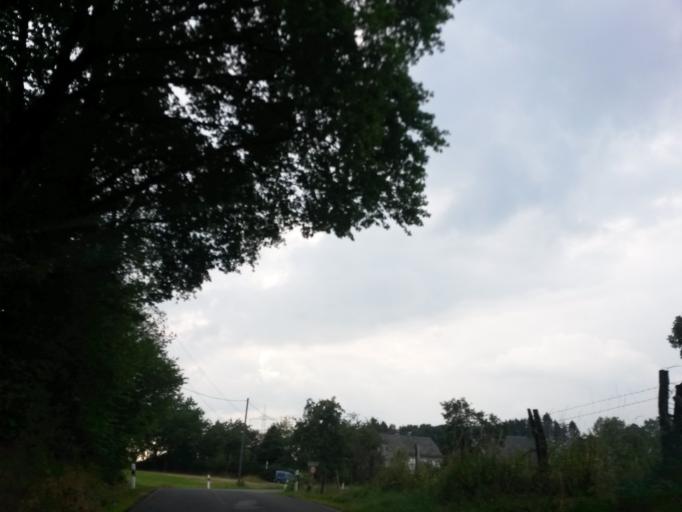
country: DE
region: North Rhine-Westphalia
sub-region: Regierungsbezirk Koln
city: Marienheide
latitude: 51.0235
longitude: 7.4857
